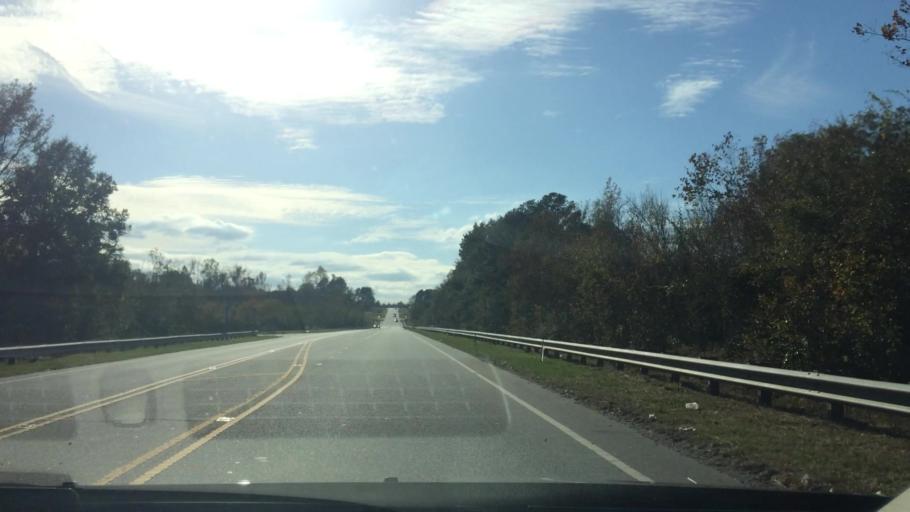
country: US
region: North Carolina
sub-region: Greene County
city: Snow Hill
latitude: 35.4578
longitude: -77.6766
